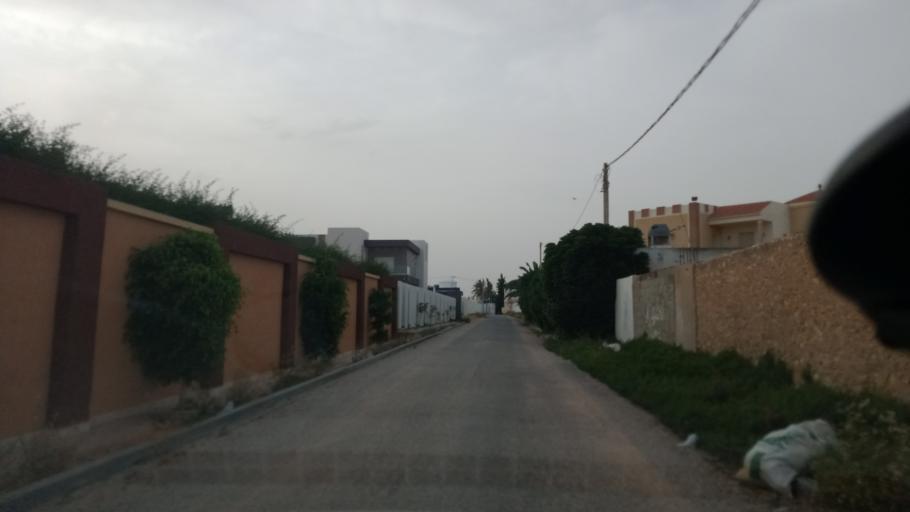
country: TN
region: Safaqis
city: Al Qarmadah
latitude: 34.7871
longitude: 10.7644
